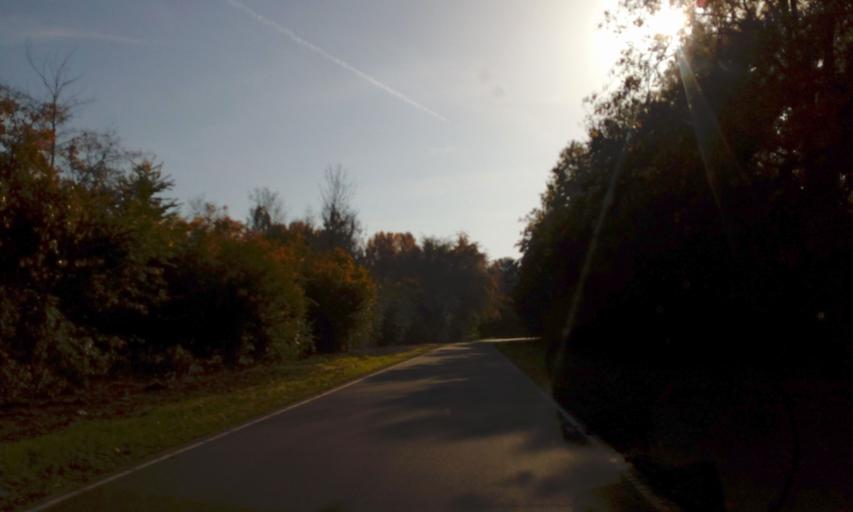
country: NL
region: South Holland
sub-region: Gemeente Lansingerland
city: Bleiswijk
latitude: 52.0147
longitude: 4.5508
